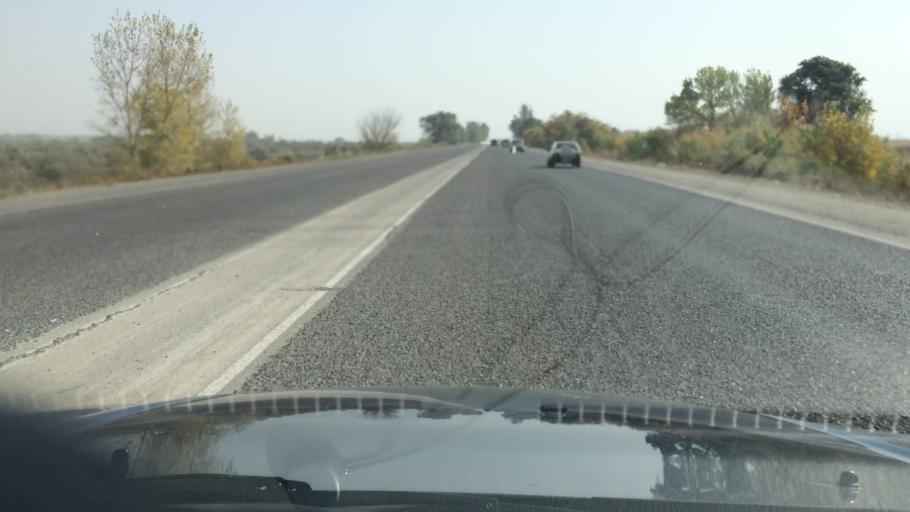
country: KG
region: Chuy
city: Kant
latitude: 42.9560
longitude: 74.9356
